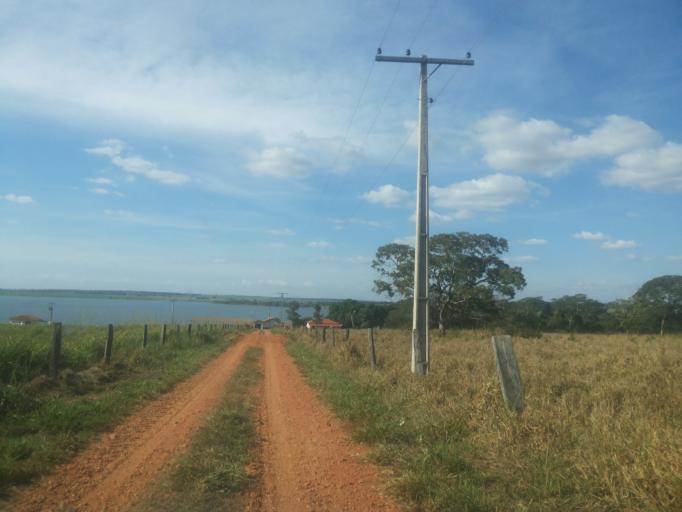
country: BR
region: Minas Gerais
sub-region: Santa Vitoria
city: Santa Vitoria
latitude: -19.0039
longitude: -50.3974
